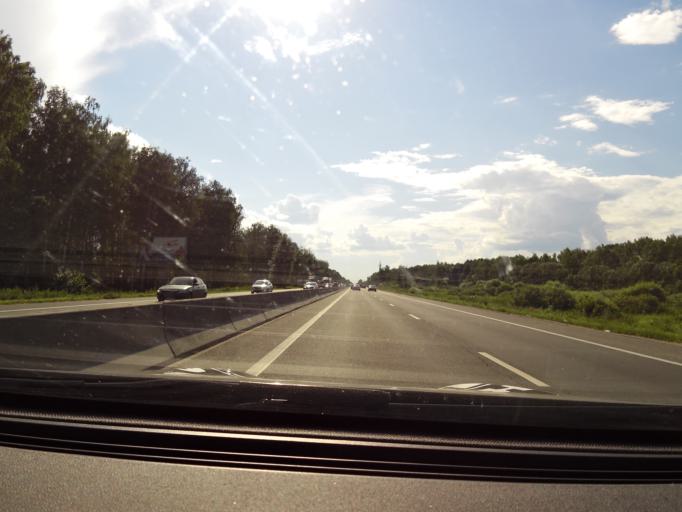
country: RU
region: Nizjnij Novgorod
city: Gorbatovka
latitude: 56.3101
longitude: 43.7792
